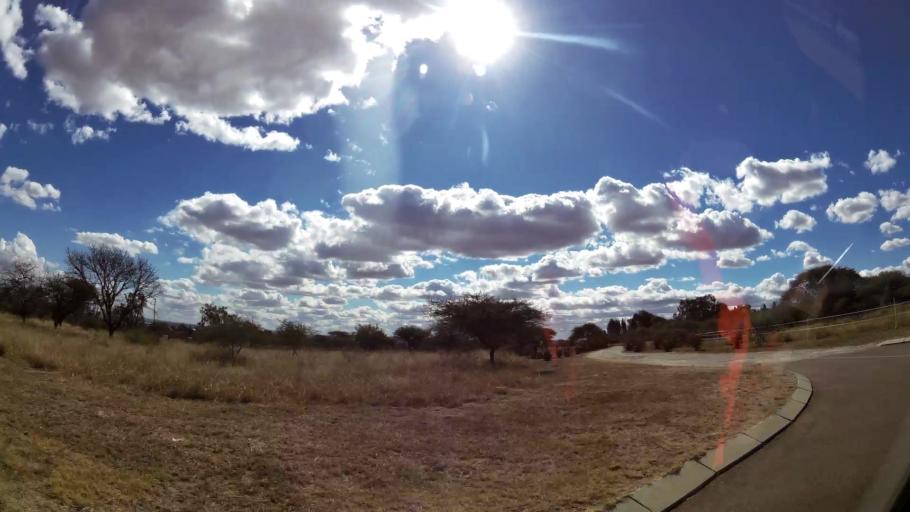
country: ZA
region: Limpopo
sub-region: Capricorn District Municipality
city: Polokwane
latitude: -23.8712
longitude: 29.4940
